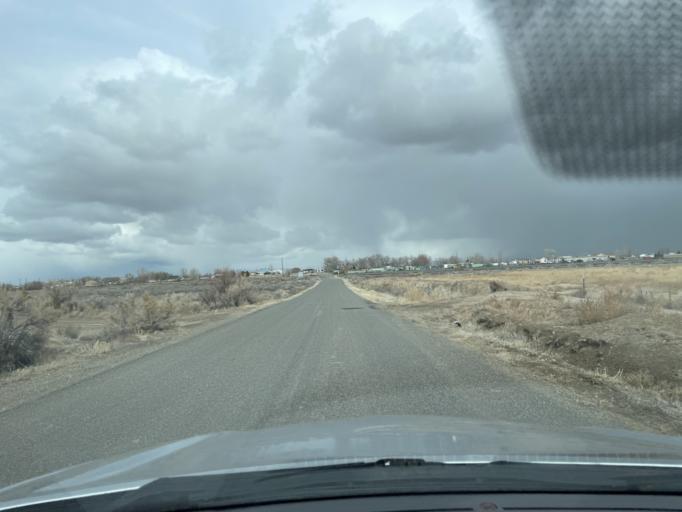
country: US
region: Colorado
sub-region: Mesa County
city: Loma
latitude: 39.1883
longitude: -108.8036
